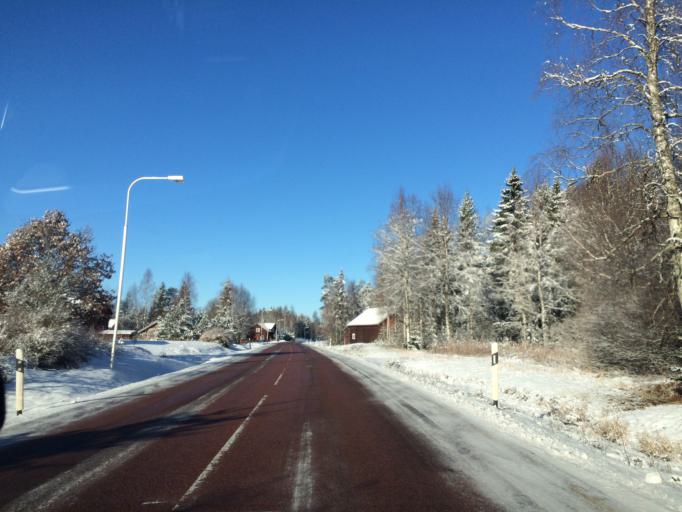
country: SE
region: Dalarna
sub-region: Vansbro Kommun
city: Vansbro
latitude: 60.8443
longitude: 14.1889
